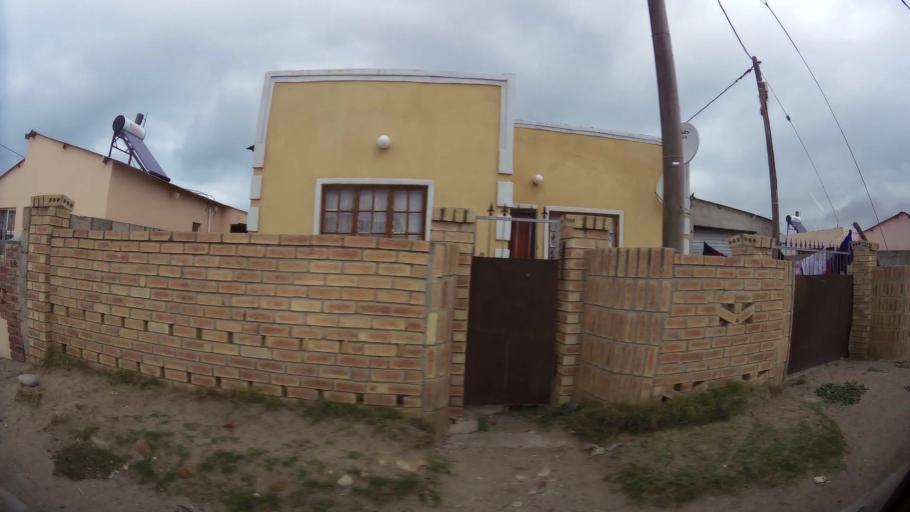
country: ZA
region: Eastern Cape
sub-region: Nelson Mandela Bay Metropolitan Municipality
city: Port Elizabeth
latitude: -33.8887
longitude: 25.5991
